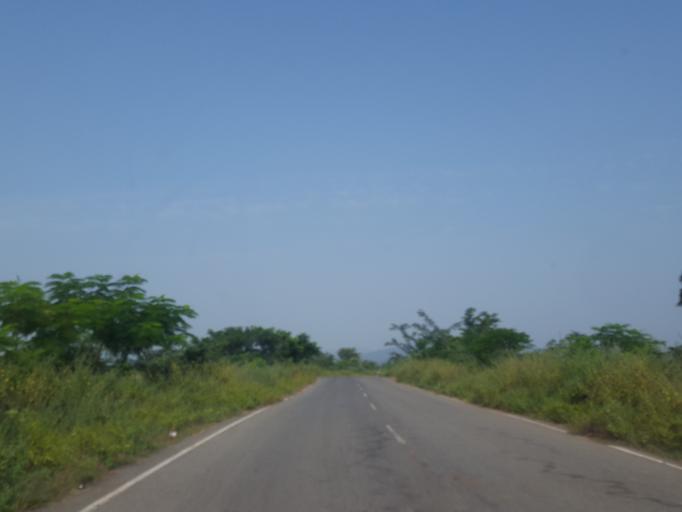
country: IN
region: Telangana
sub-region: Khammam
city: Yellandu
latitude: 17.6522
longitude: 80.2827
